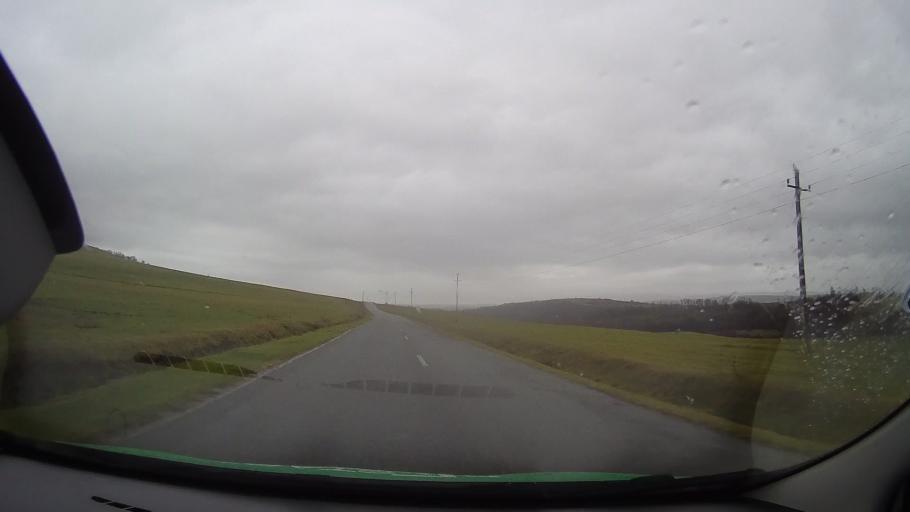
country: RO
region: Mures
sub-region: Comuna Brancovenesti
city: Valenii de Mures
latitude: 46.9121
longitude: 24.7824
